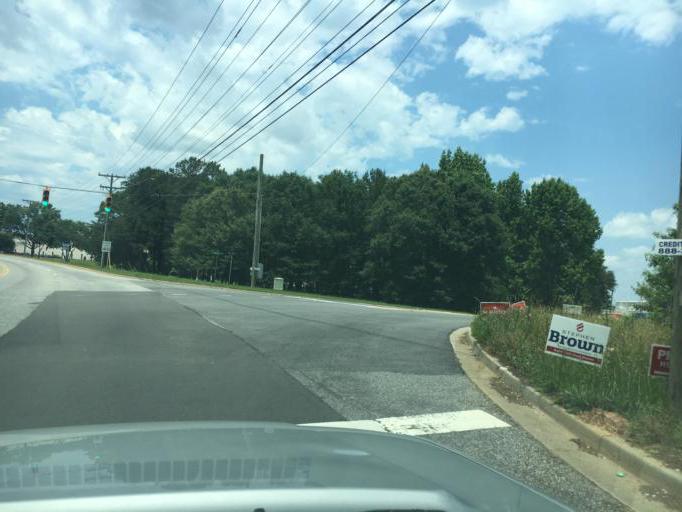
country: US
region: South Carolina
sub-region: Greenville County
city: Five Forks
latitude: 34.8529
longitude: -82.2321
